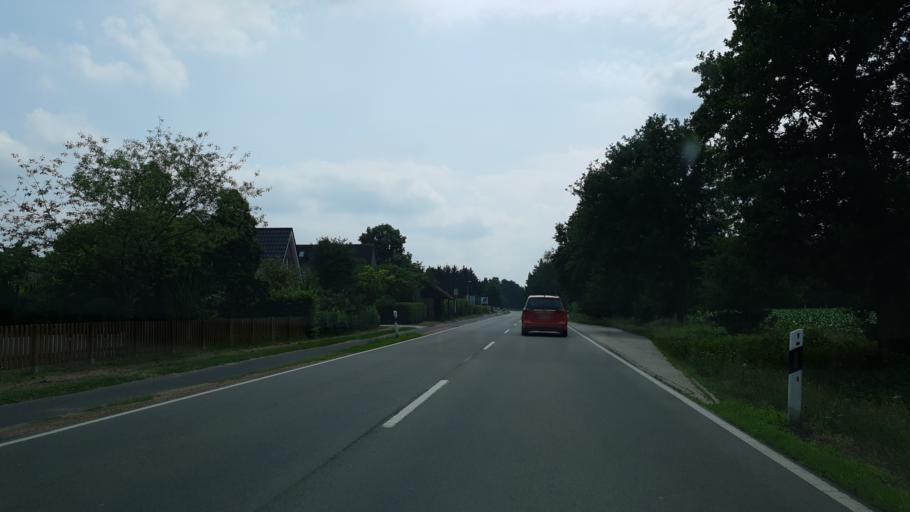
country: DE
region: Lower Saxony
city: Geeste
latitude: 52.5654
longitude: 7.2053
